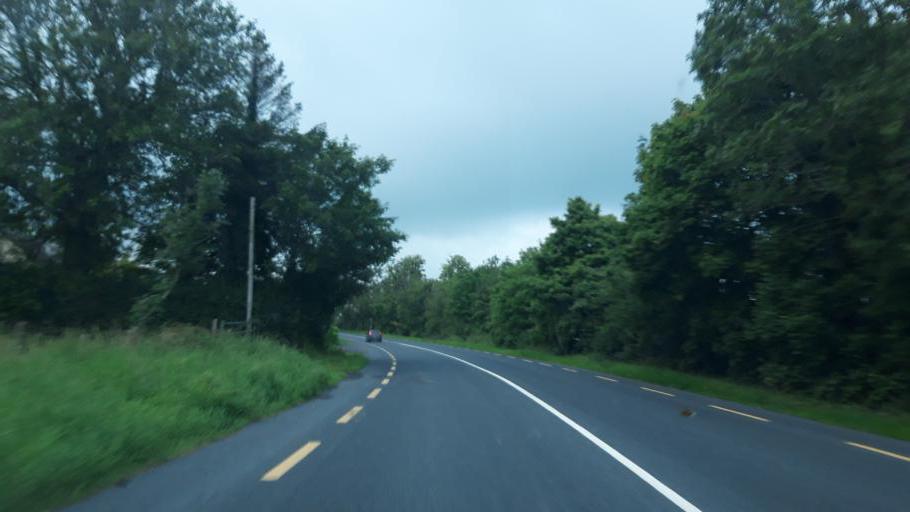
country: IE
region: Leinster
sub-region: Kilkenny
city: Thomastown
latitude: 52.5464
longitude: -7.1303
